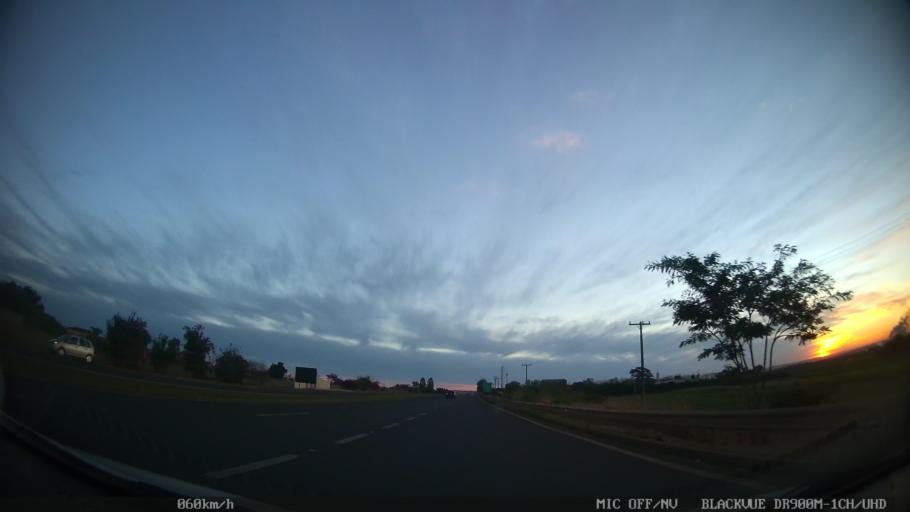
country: BR
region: Sao Paulo
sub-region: Catanduva
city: Catanduva
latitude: -21.1095
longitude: -48.9644
